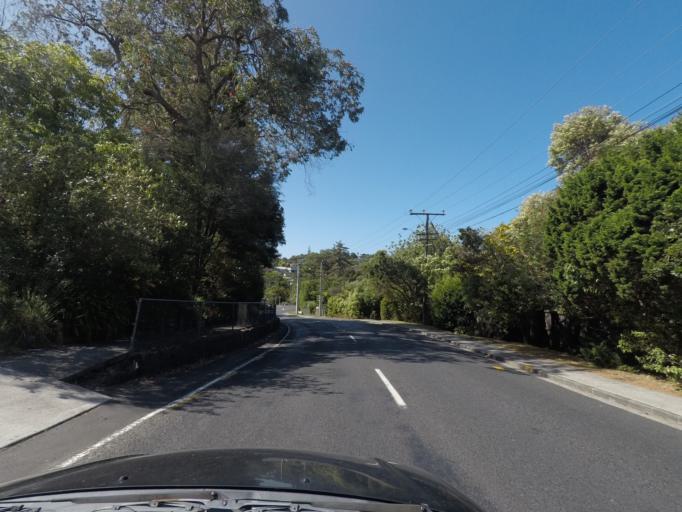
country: NZ
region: Auckland
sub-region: Auckland
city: Waitakere
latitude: -36.9253
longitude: 174.6554
